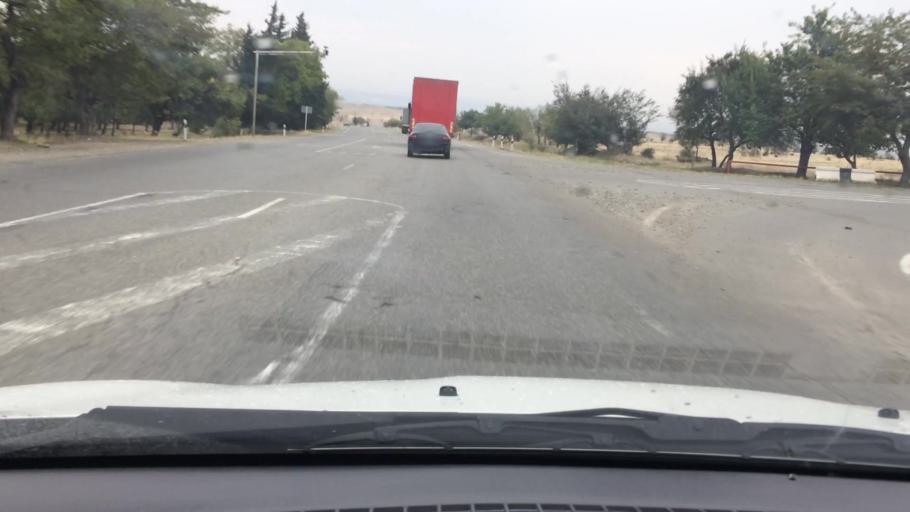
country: GE
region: T'bilisi
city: Tbilisi
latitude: 41.6394
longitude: 44.8684
